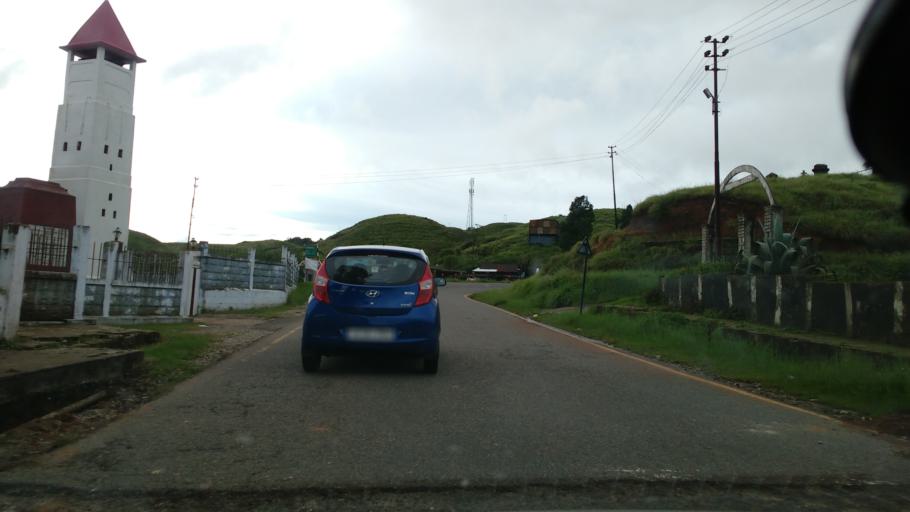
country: IN
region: Meghalaya
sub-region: East Khasi Hills
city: Cherrapunji
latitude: 25.2767
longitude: 91.7304
